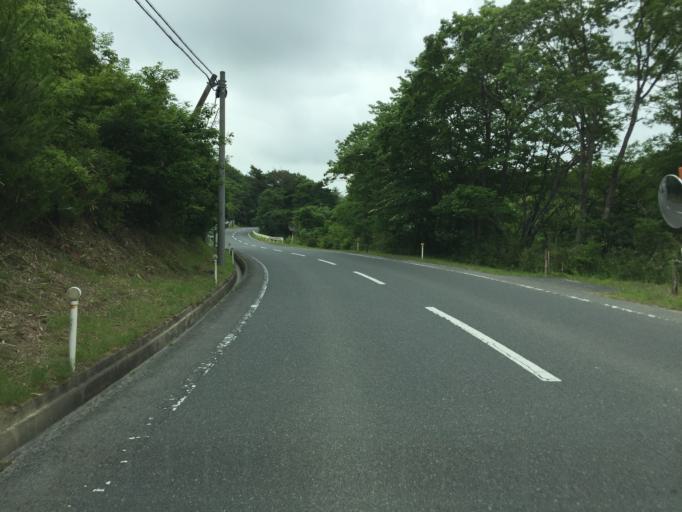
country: JP
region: Miyagi
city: Marumori
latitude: 37.7512
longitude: 140.9602
